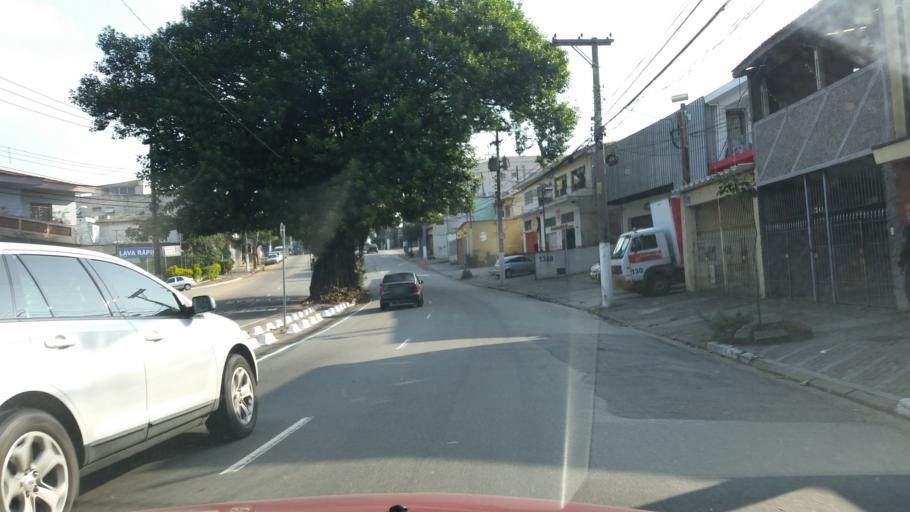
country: BR
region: Sao Paulo
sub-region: Diadema
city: Diadema
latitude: -23.6378
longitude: -46.6553
